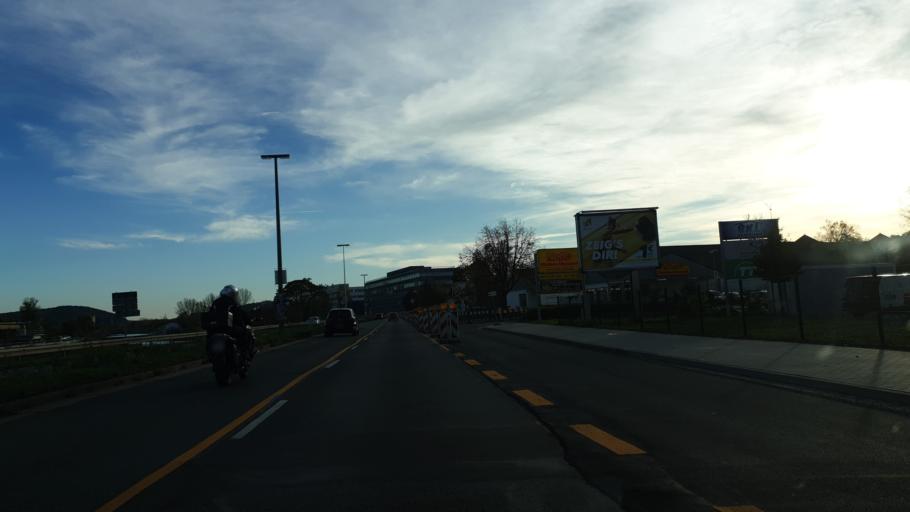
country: DE
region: Thuringia
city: Gera
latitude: 50.8608
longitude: 12.0773
